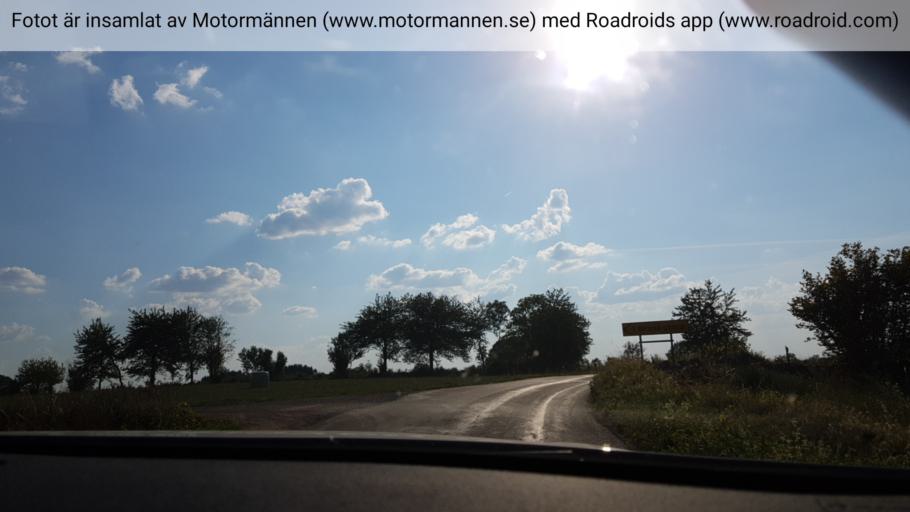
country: SE
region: Vaestra Goetaland
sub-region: Skovde Kommun
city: Stopen
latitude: 58.4948
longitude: 13.7932
